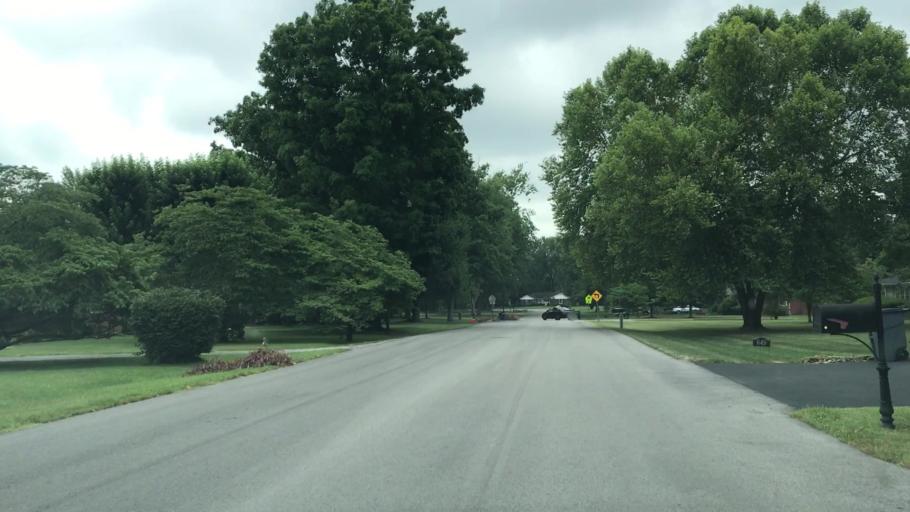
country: US
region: Kentucky
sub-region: Warren County
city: Bowling Green
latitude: 36.9868
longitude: -86.4153
